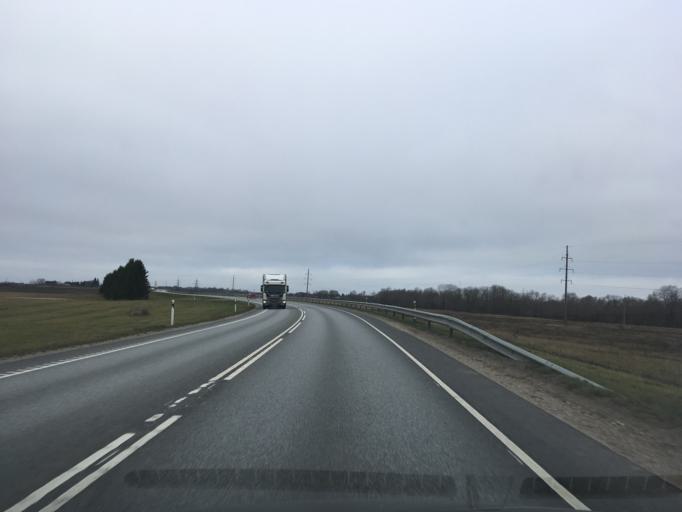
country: EE
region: Ida-Virumaa
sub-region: Narva-Joesuu linn
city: Narva-Joesuu
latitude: 59.4036
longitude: 28.0522
